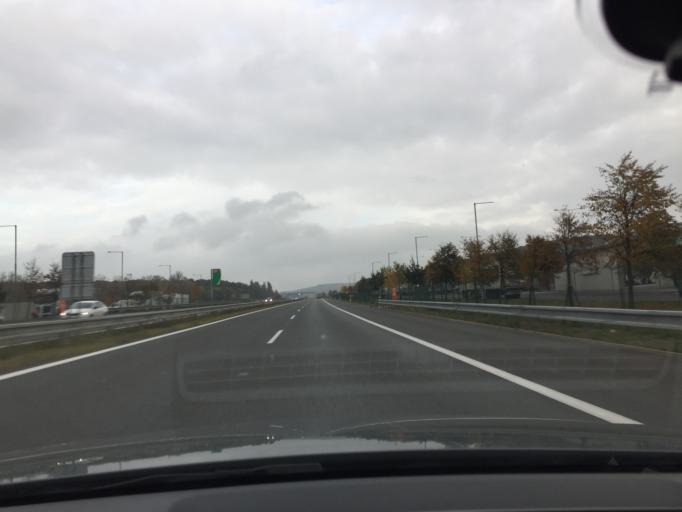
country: CZ
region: Ustecky
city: Chlumec
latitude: 50.7122
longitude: 13.9687
